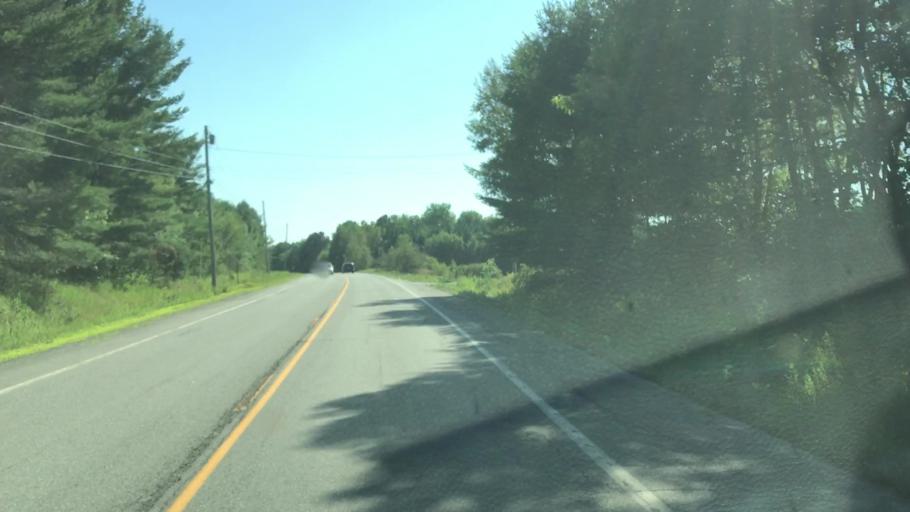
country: US
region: Maine
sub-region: Penobscot County
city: Enfield
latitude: 45.3275
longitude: -68.5916
